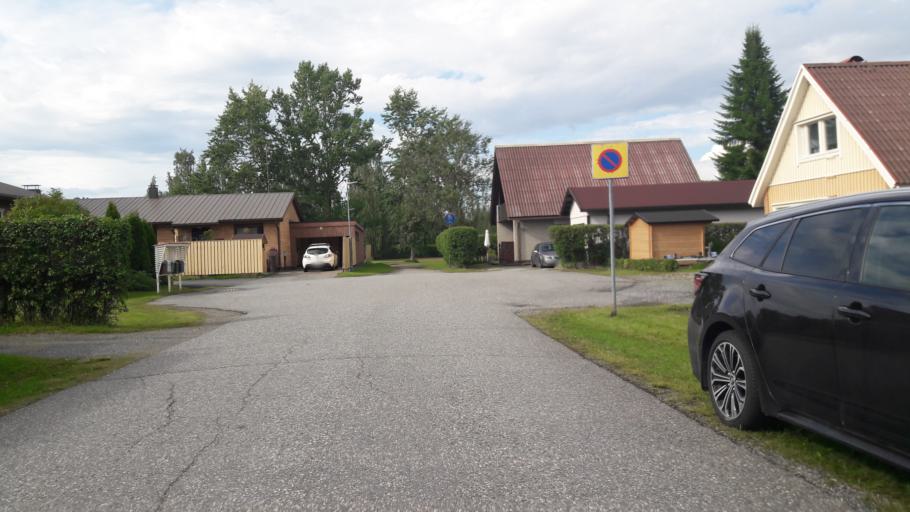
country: FI
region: North Karelia
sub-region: Joensuu
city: Joensuu
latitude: 62.5781
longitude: 29.8127
